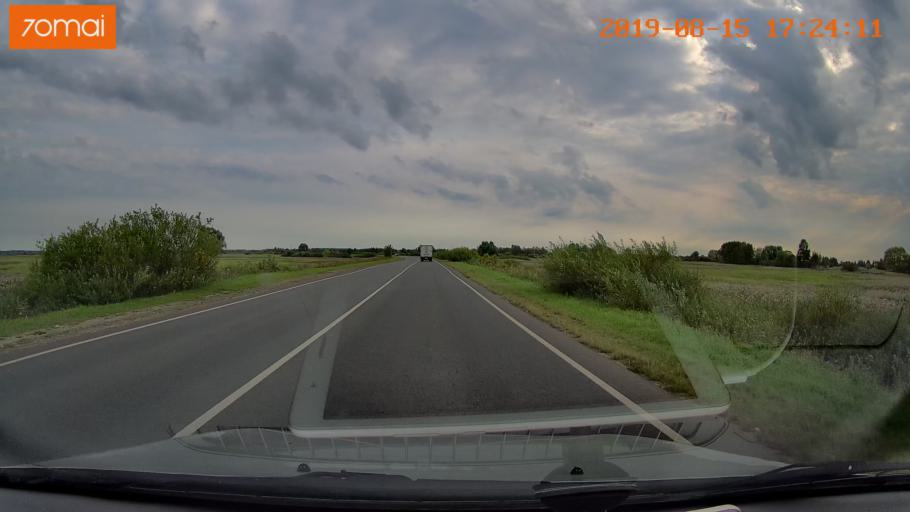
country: RU
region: Moskovskaya
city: Ashitkovo
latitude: 55.3905
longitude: 38.5548
